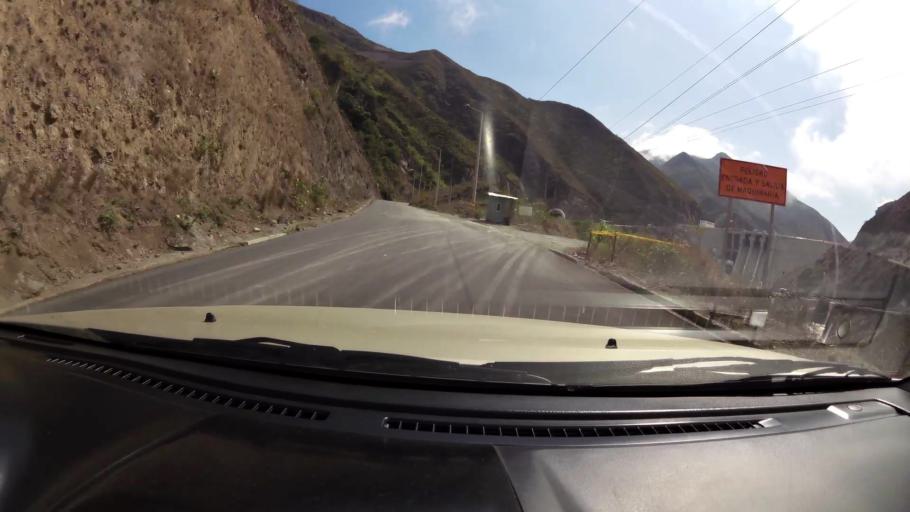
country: EC
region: El Oro
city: Pasaje
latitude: -3.3141
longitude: -79.4865
